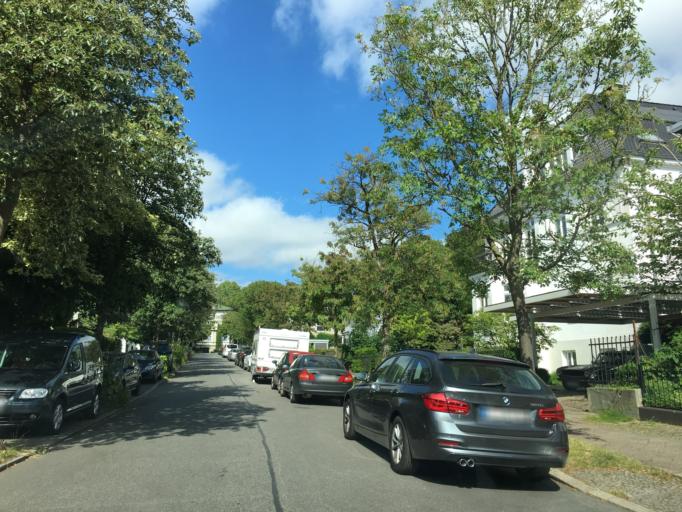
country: DE
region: Schleswig-Holstein
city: Kiel
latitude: 54.3386
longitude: 10.1470
